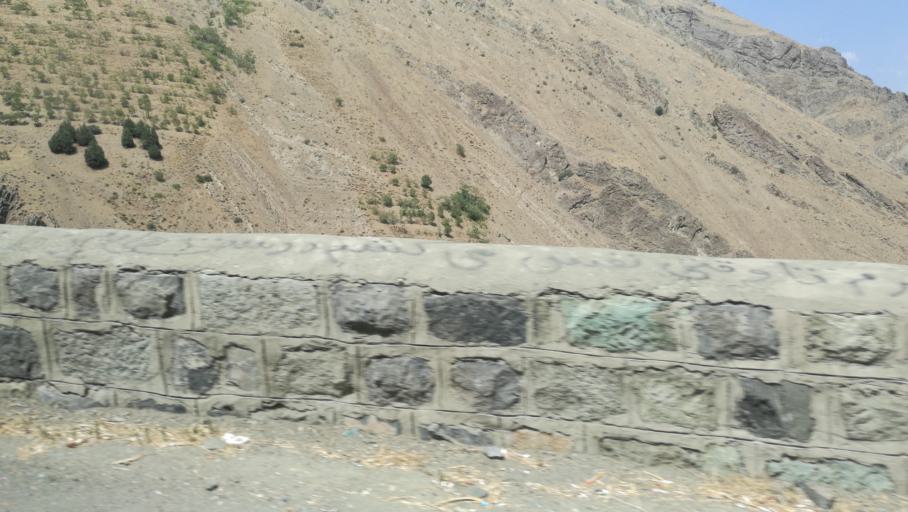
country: IR
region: Alborz
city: Karaj
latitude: 35.9804
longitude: 51.0927
